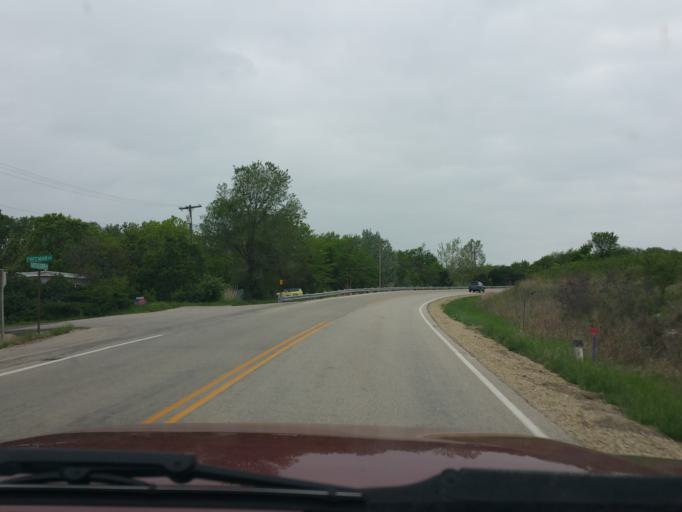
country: US
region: Kansas
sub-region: Riley County
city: Manhattan
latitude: 39.2493
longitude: -96.6081
